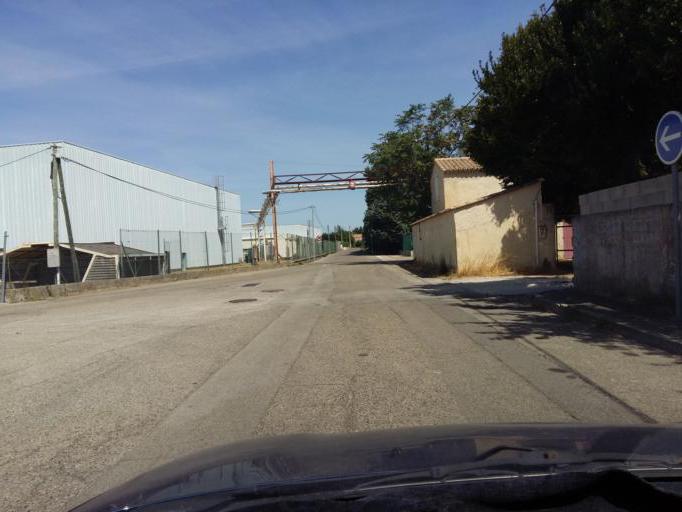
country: FR
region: Provence-Alpes-Cote d'Azur
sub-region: Departement du Vaucluse
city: Camaret-sur-Aigues
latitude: 44.1642
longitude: 4.8677
